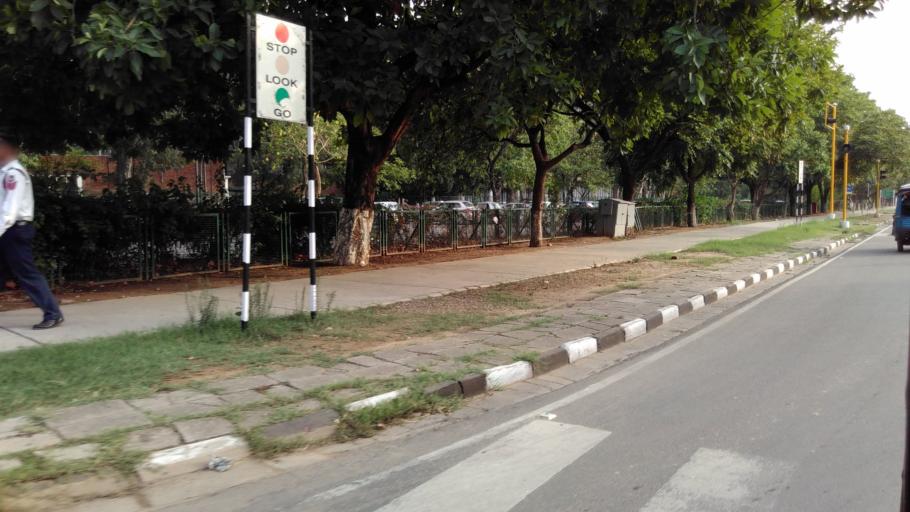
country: IN
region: Chandigarh
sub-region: Chandigarh
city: Chandigarh
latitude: 30.7502
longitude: 76.7915
